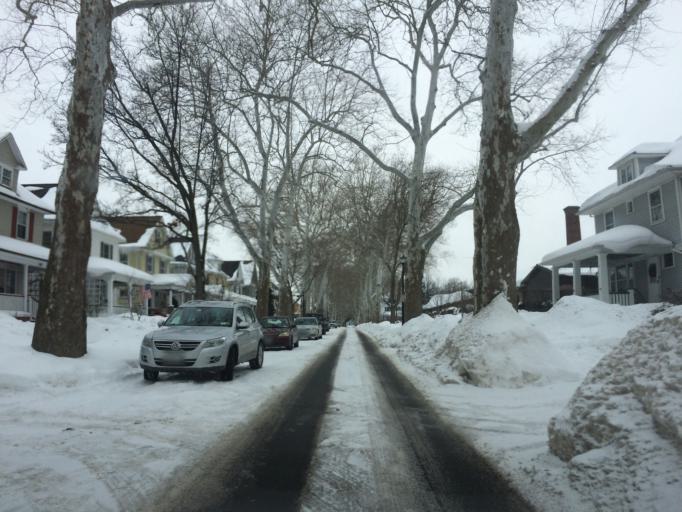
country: US
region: New York
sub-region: Monroe County
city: Rochester
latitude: 43.1361
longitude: -77.5993
